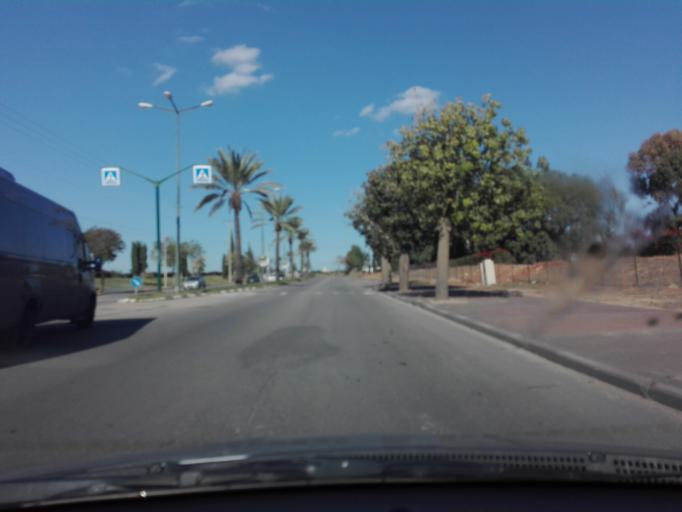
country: IL
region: Central District
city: Netanya
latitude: 32.3029
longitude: 34.8547
